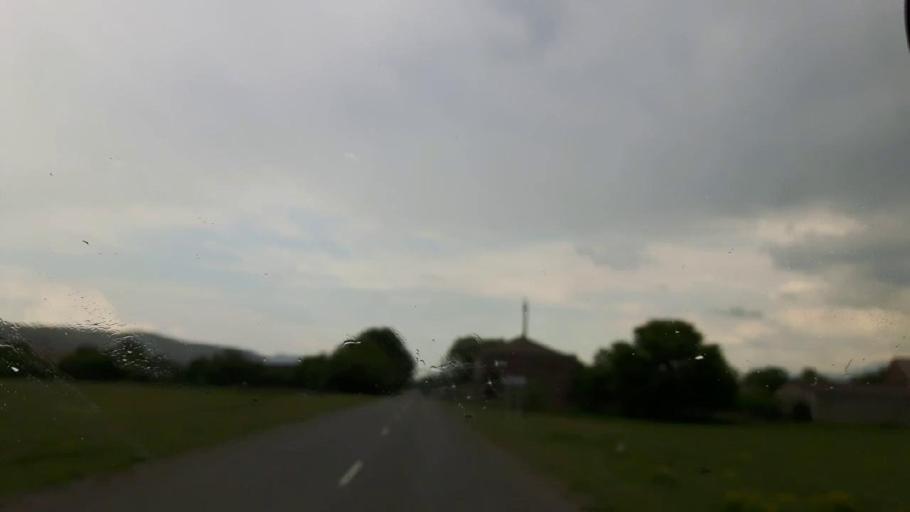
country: GE
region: Shida Kartli
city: Gori
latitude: 41.9625
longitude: 44.1937
